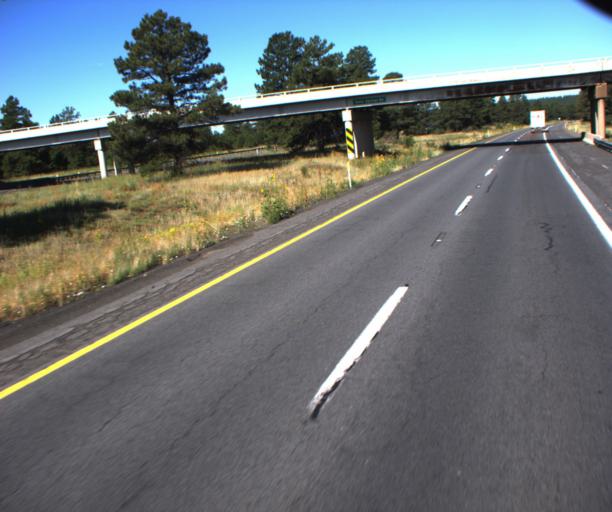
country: US
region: Arizona
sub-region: Coconino County
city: Parks
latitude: 35.2479
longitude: -111.9784
